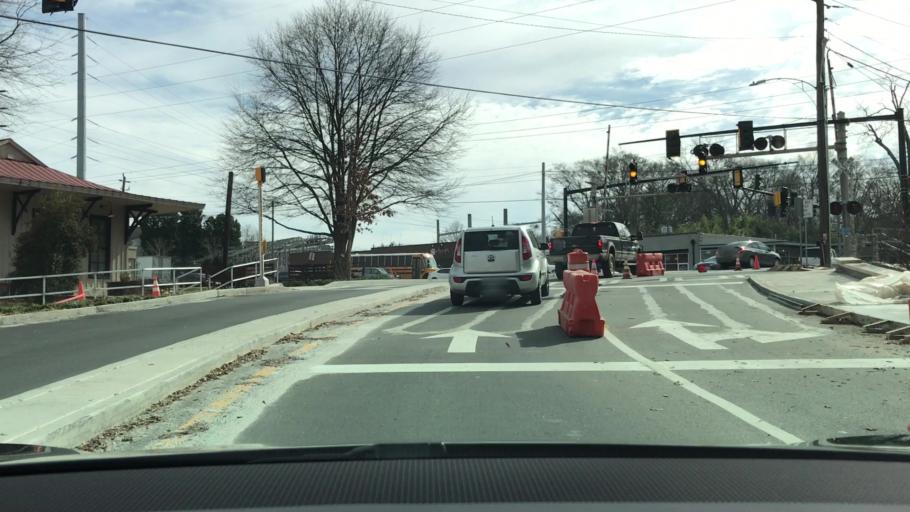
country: US
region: Georgia
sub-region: DeKalb County
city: Decatur
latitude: 33.7716
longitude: -84.2930
